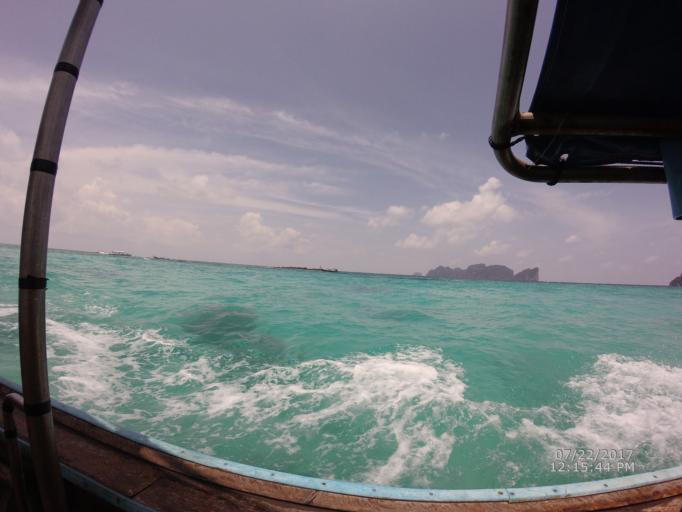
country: TH
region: Krabi
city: Saladan
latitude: 7.7272
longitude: 98.7883
